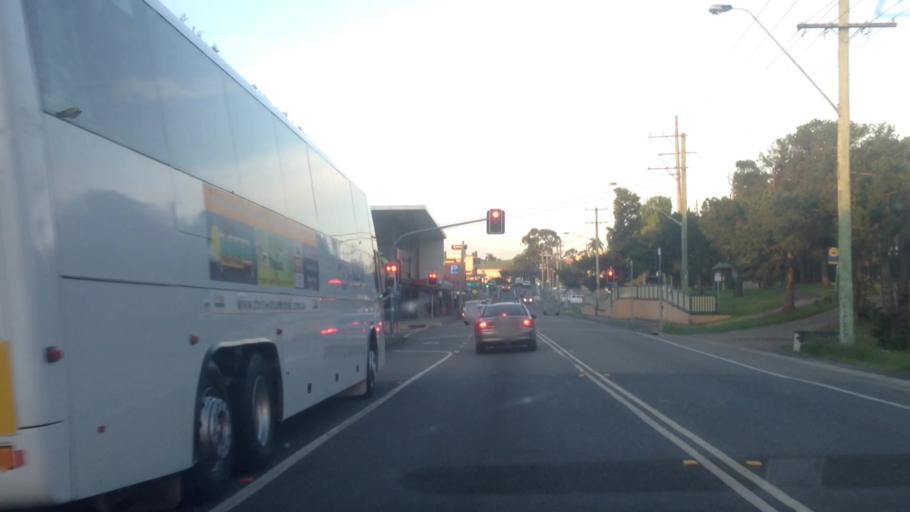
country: AU
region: New South Wales
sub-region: Lake Macquarie Shire
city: Dora Creek
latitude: -33.1101
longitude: 151.4854
